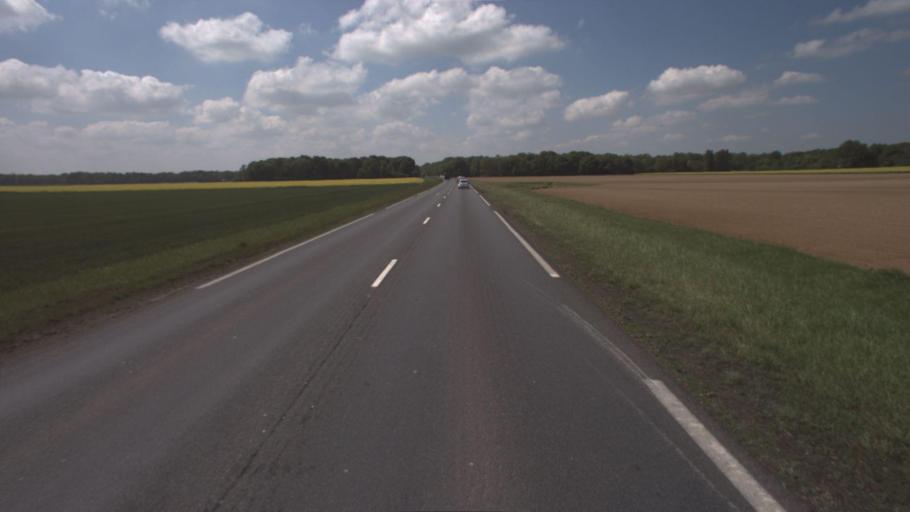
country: FR
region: Ile-de-France
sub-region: Departement de Seine-et-Marne
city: Chaumes-en-Brie
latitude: 48.7015
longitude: 2.8290
